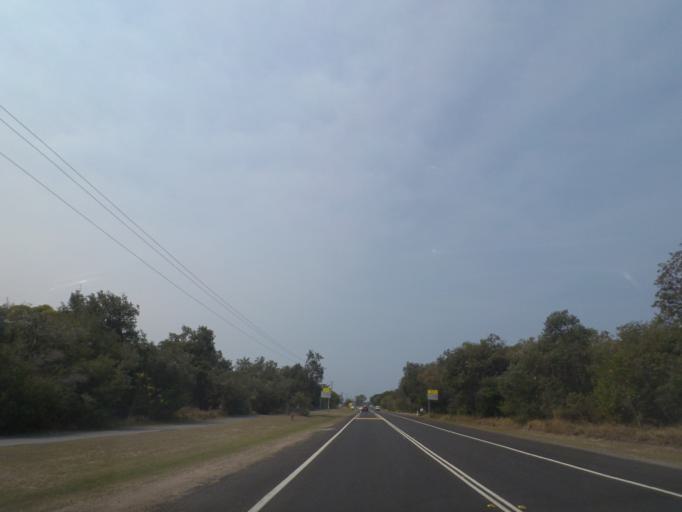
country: AU
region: New South Wales
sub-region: Tweed
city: Casuarina
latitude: -28.3407
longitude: 153.5719
